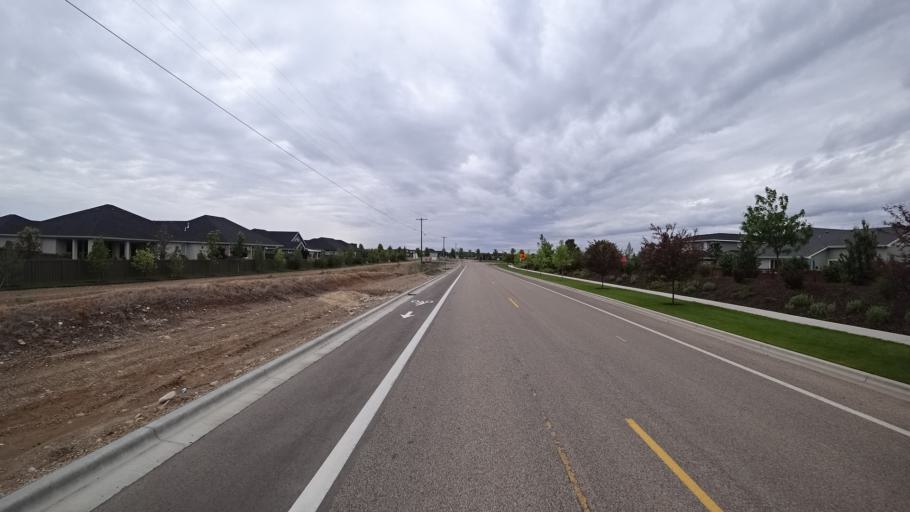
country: US
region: Idaho
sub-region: Ada County
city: Eagle
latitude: 43.7089
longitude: -116.4236
